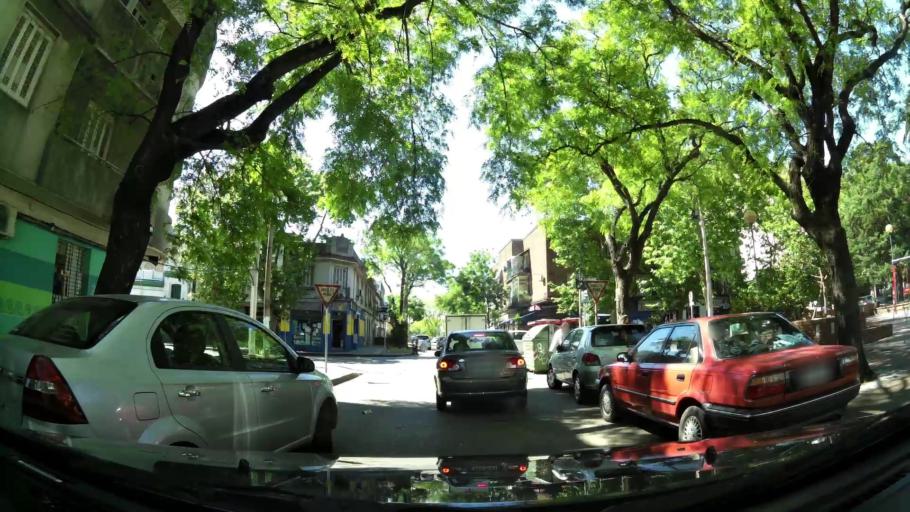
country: UY
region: Montevideo
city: Montevideo
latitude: -34.9025
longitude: -56.1422
